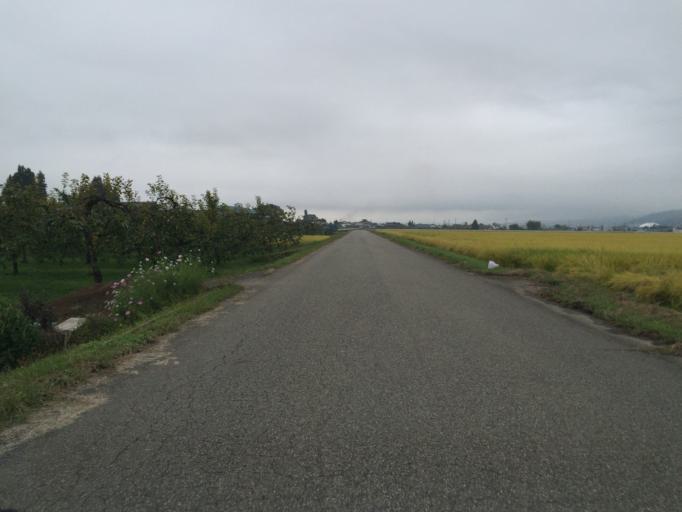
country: JP
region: Fukushima
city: Kitakata
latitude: 37.4428
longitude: 139.9161
